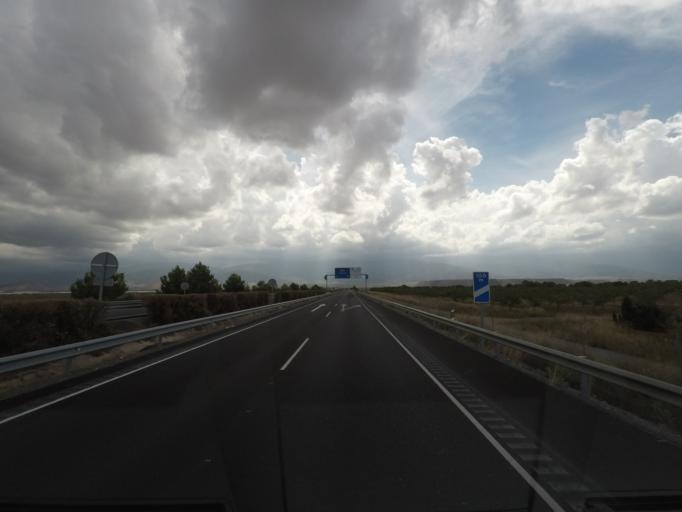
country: ES
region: Andalusia
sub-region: Provincia de Granada
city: Albunan
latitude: 37.2365
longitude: -3.0822
